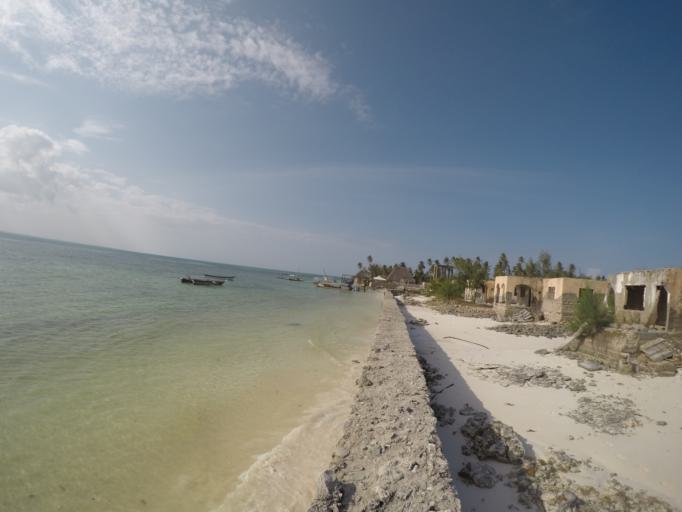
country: TZ
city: Kiwengwa
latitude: -6.1443
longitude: 39.4892
